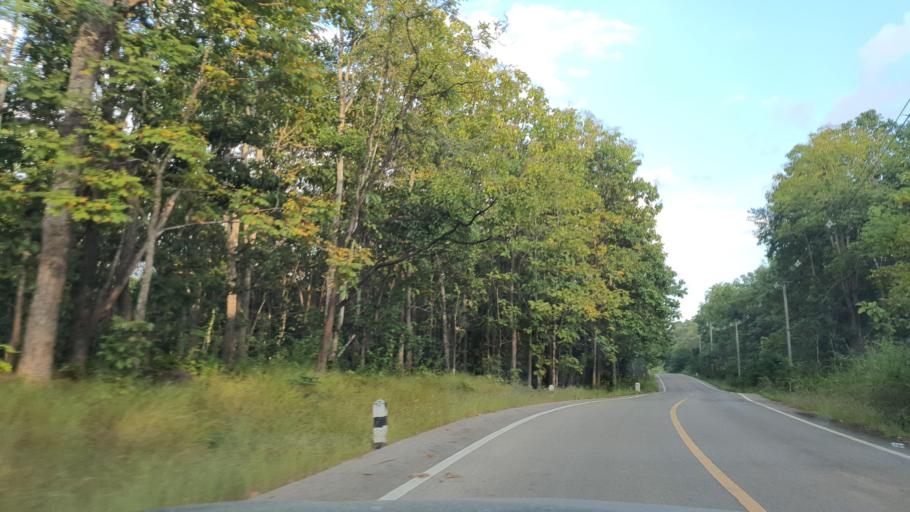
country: TH
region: Chiang Mai
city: Mae On
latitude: 18.8547
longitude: 99.2517
